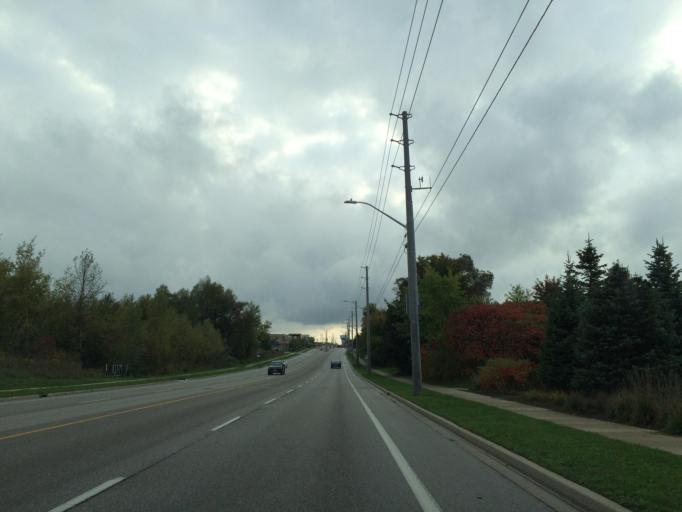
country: CA
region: Ontario
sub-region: Wellington County
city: Guelph
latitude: 43.5045
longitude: -80.1836
